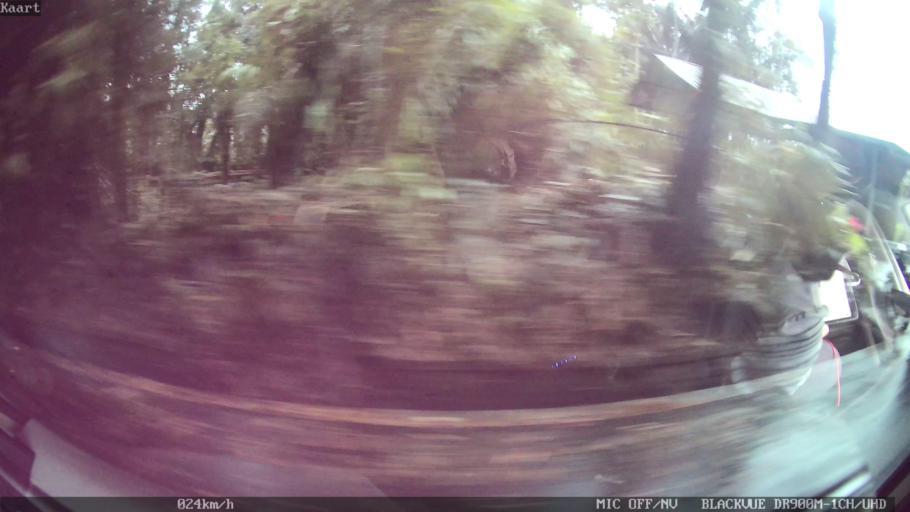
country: ID
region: Bali
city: Banjar Teguan
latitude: -8.5032
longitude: 115.2313
